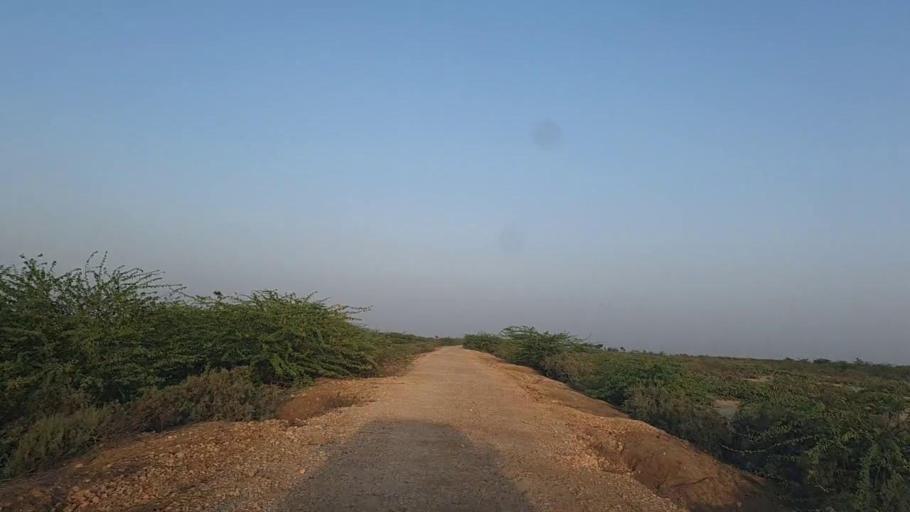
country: PK
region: Sindh
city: Naukot
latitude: 24.6978
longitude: 69.2542
